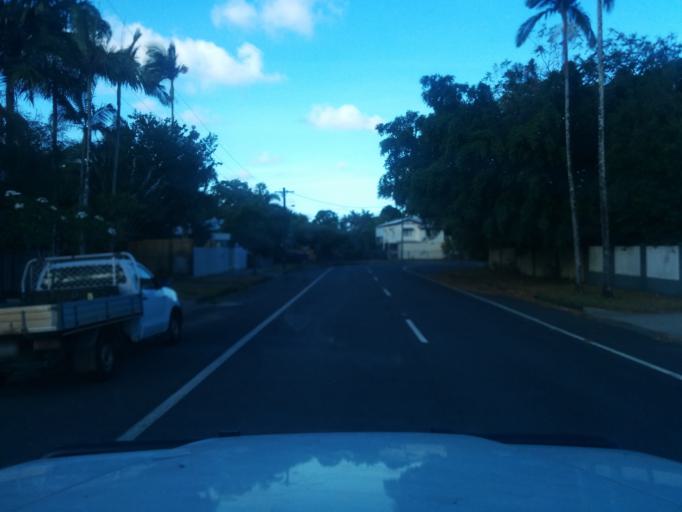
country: AU
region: Queensland
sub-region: Cairns
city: Woree
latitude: -16.9398
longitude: 145.7401
